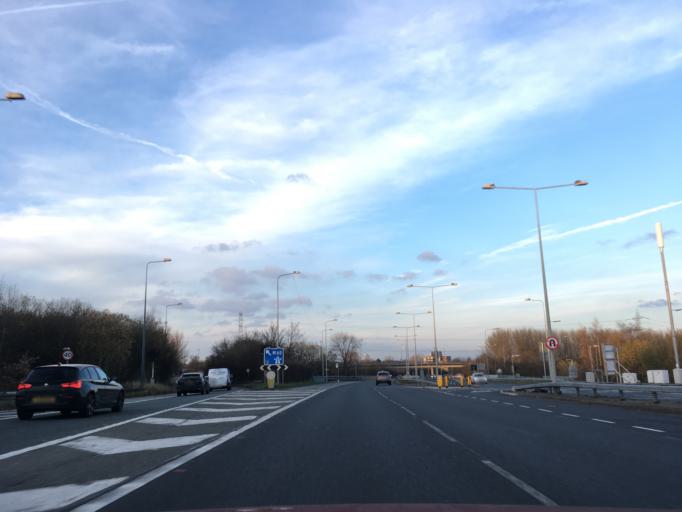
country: GB
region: England
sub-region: Manchester
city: Didsbury
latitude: 53.3970
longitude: -2.2266
